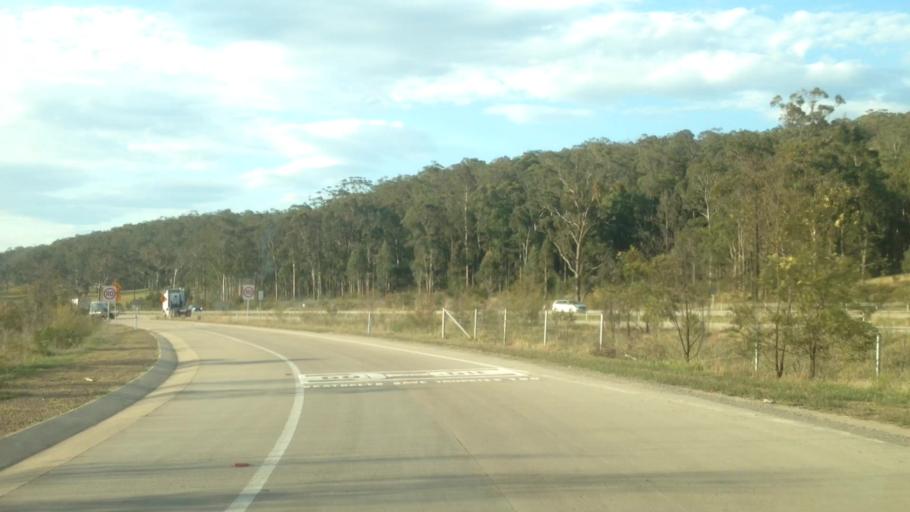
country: AU
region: New South Wales
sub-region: Cessnock
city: Heddon Greta
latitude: -32.8434
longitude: 151.5421
